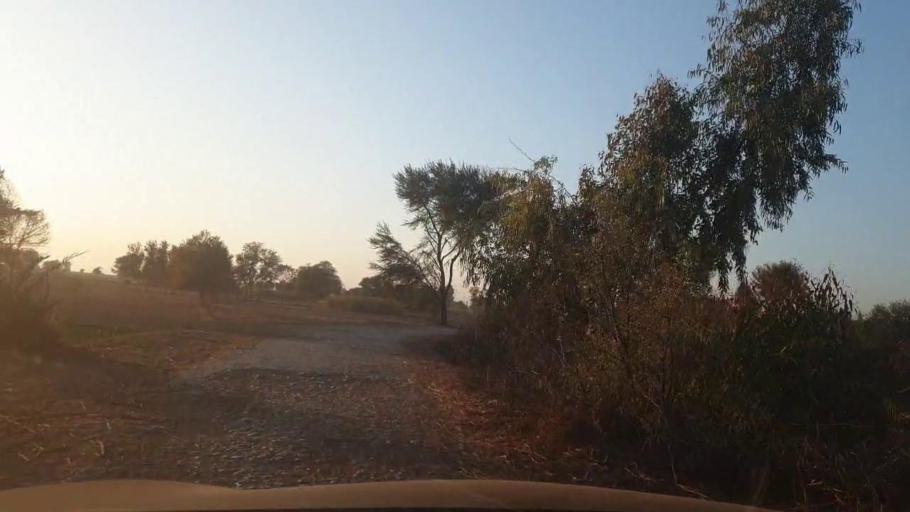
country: PK
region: Sindh
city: Ubauro
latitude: 28.1834
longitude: 69.6025
